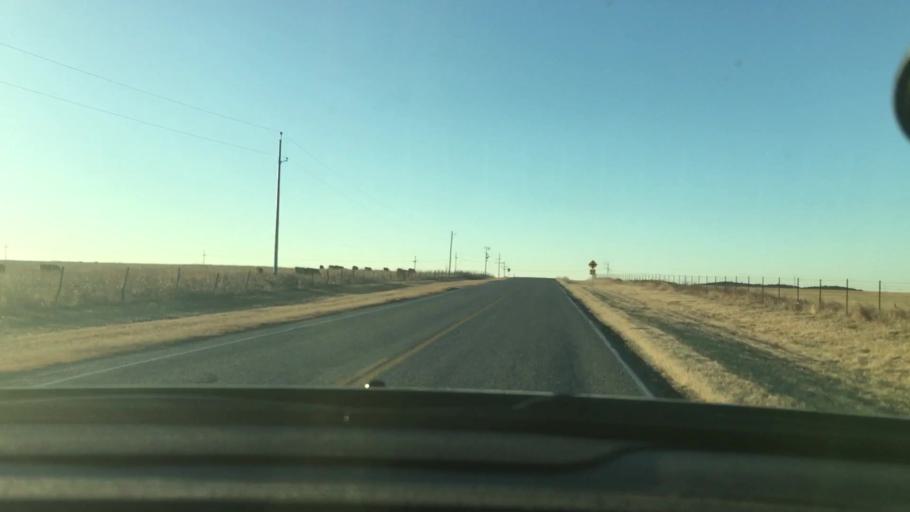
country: US
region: Oklahoma
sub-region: Murray County
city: Davis
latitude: 34.4802
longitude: -97.0907
